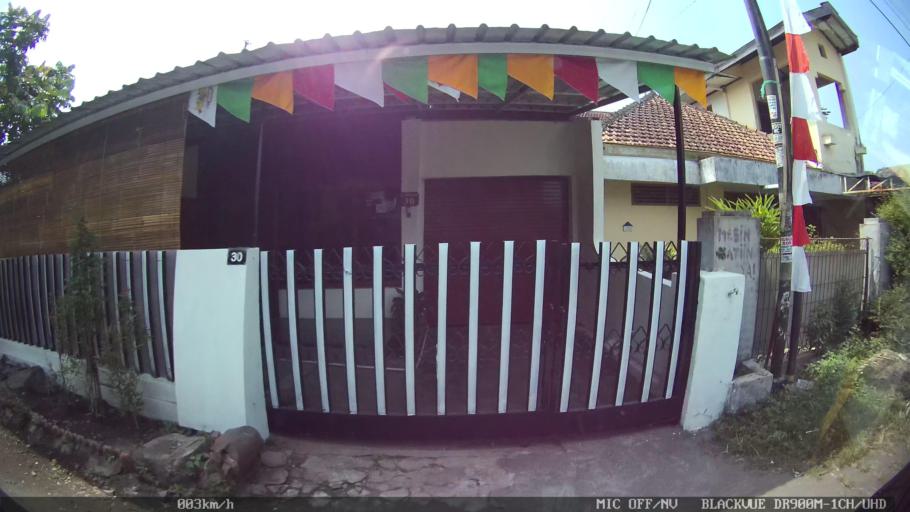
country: ID
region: Daerah Istimewa Yogyakarta
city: Yogyakarta
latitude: -7.7996
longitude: 110.3879
